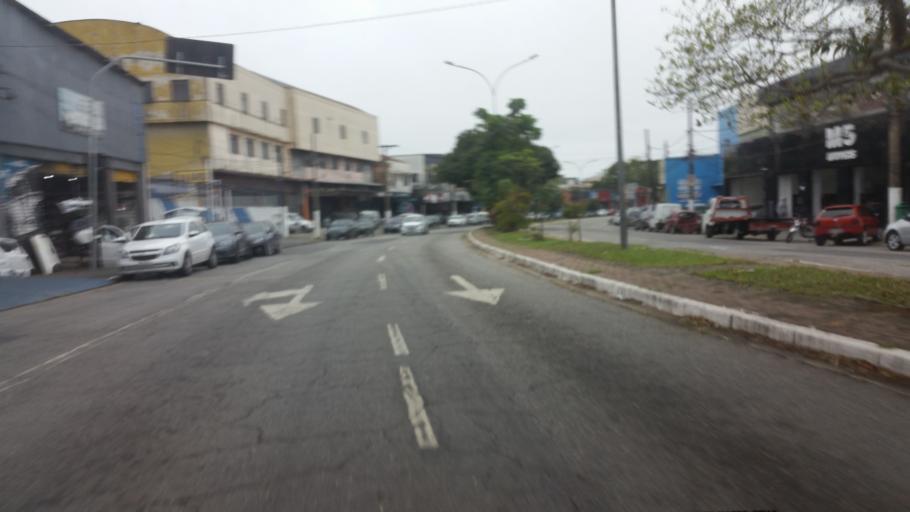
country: BR
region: Sao Paulo
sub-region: Diadema
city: Diadema
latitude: -23.6204
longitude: -46.6208
